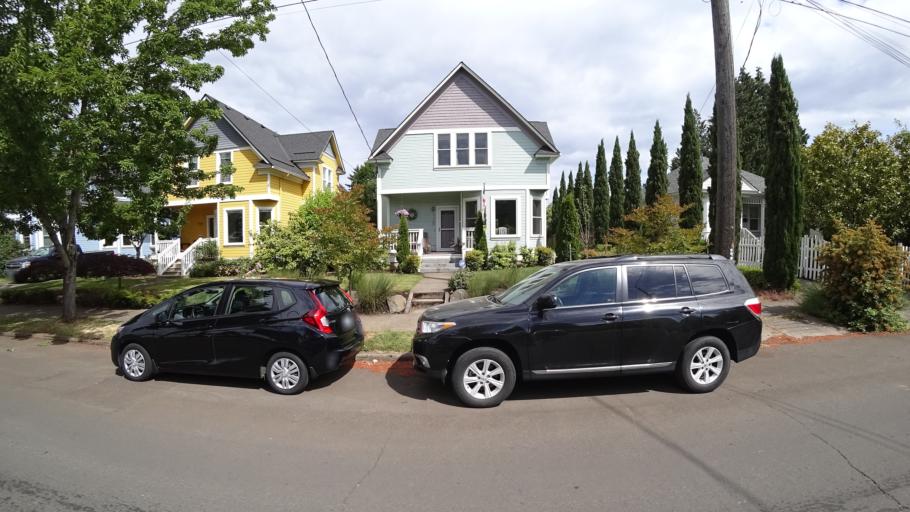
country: US
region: Oregon
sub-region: Washington County
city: West Haven
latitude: 45.5862
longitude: -122.7483
